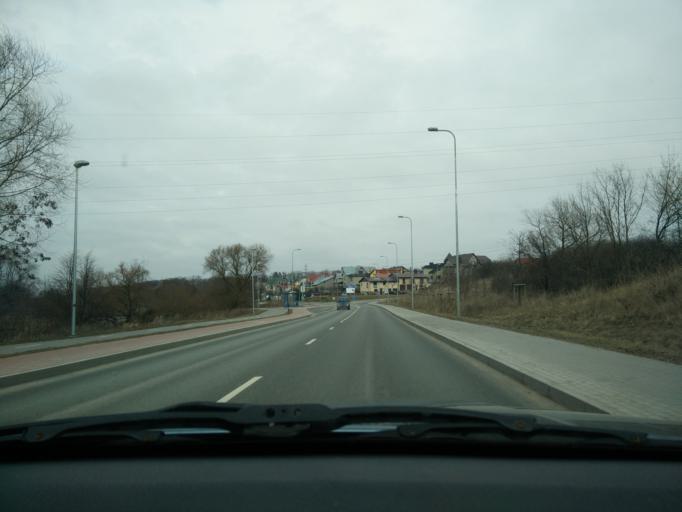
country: LT
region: Klaipedos apskritis
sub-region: Klaipeda
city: Klaipeda
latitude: 55.7169
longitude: 21.1677
